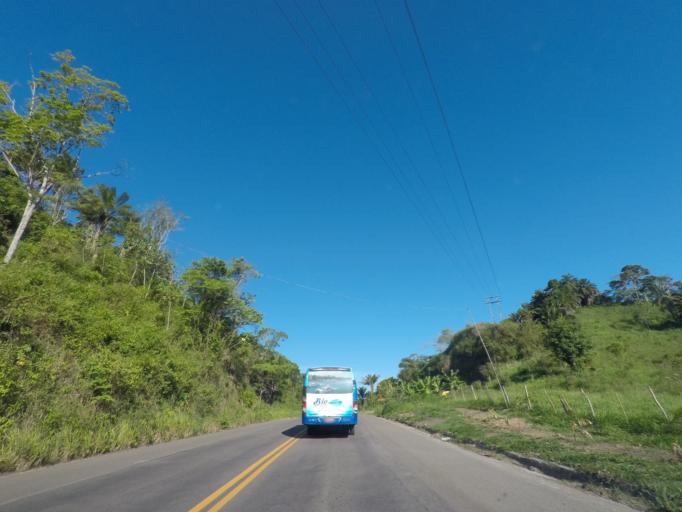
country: BR
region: Bahia
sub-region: Nazare
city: Nazare
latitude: -13.0288
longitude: -39.0122
